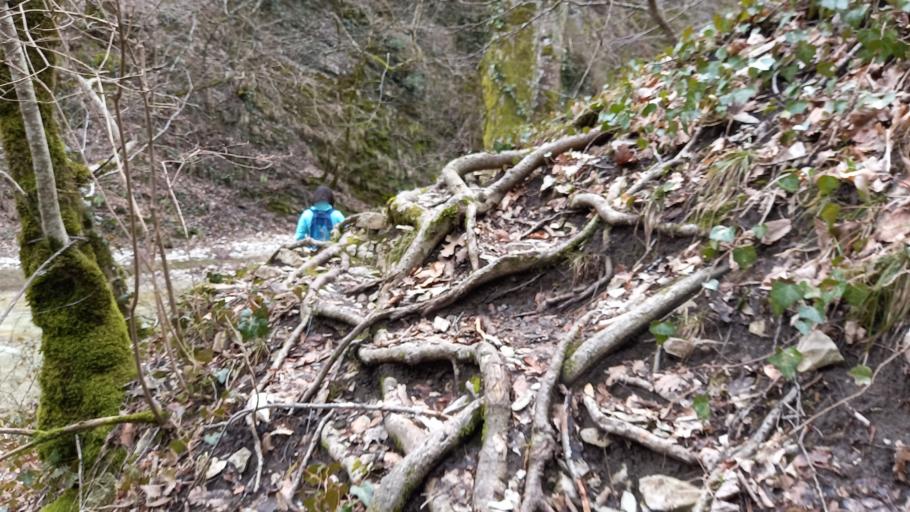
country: RU
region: Krasnodarskiy
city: Dzhubga
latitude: 44.4000
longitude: 38.7001
